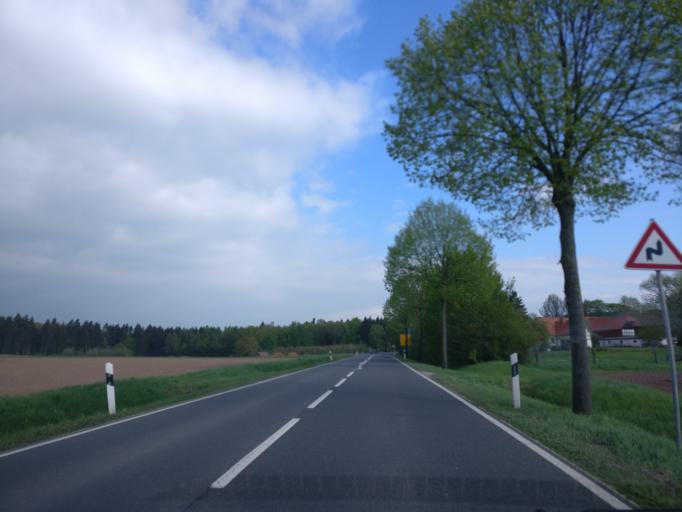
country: DE
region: Lower Saxony
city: Scheden
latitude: 51.4803
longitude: 9.7221
